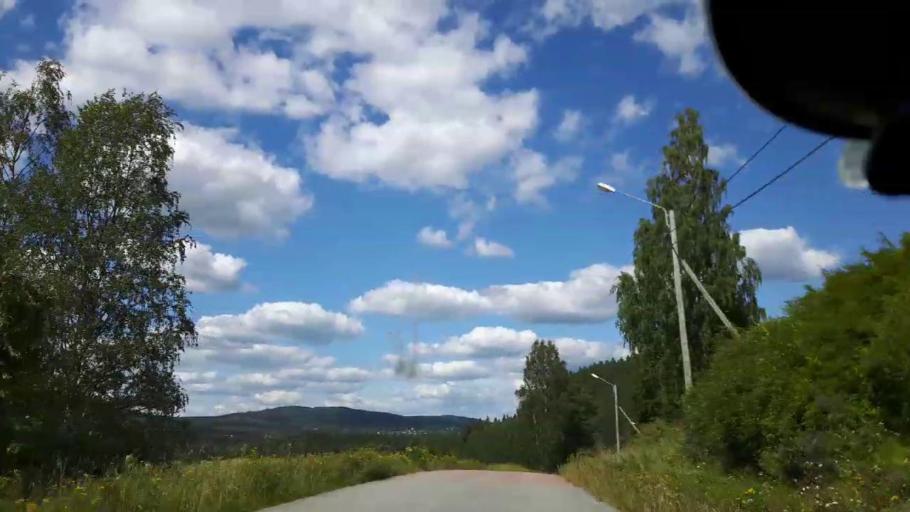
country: SE
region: Jaemtland
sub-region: Ragunda Kommun
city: Hammarstrand
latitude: 62.9541
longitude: 16.6845
